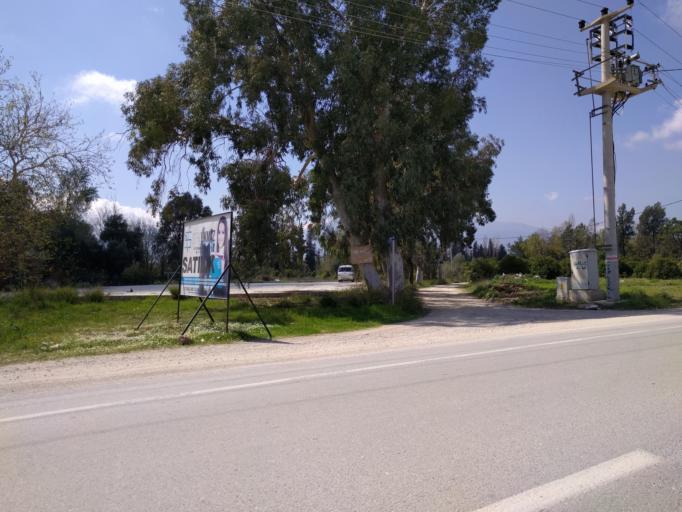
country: TR
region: Antalya
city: Cakirlar
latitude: 36.8935
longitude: 30.6008
